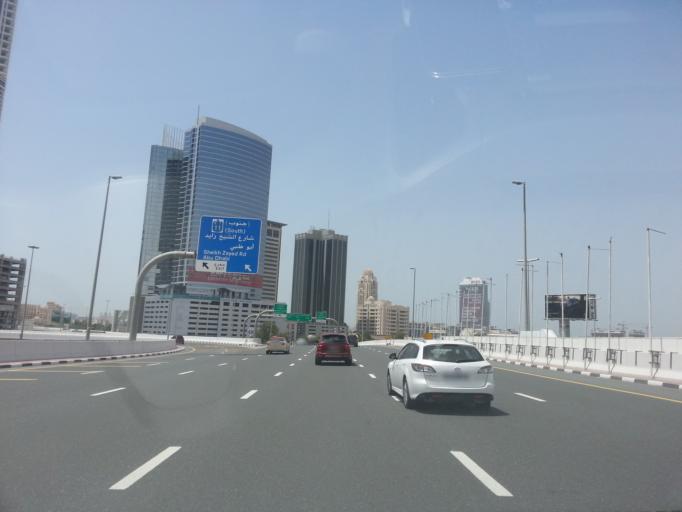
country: AE
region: Dubai
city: Dubai
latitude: 25.0860
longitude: 55.1542
